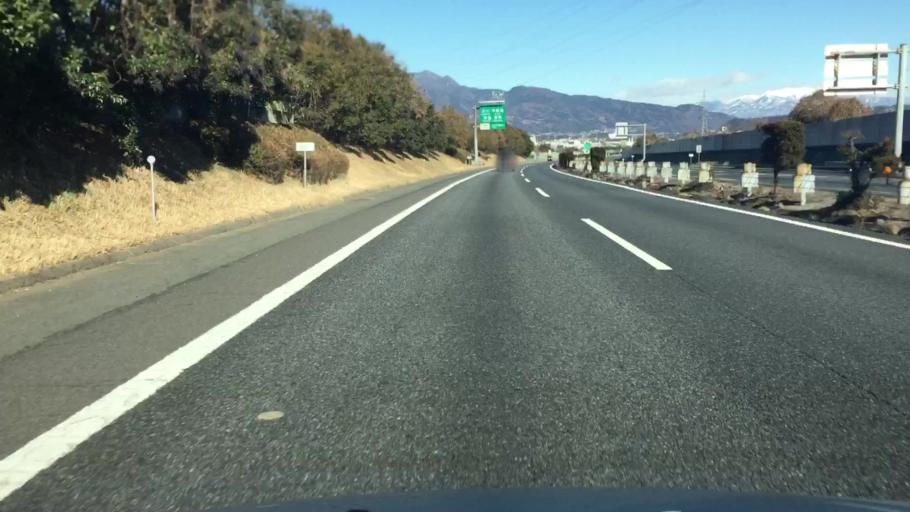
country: JP
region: Gunma
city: Shibukawa
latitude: 36.4644
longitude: 139.0115
